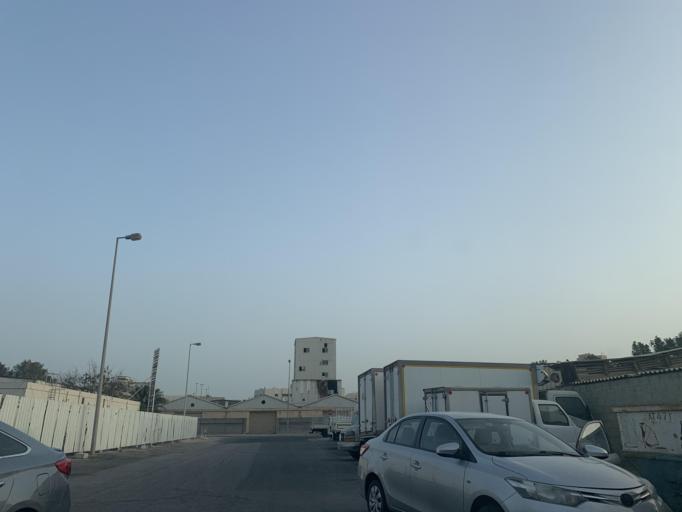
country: BH
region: Manama
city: Manama
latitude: 26.1966
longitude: 50.5939
